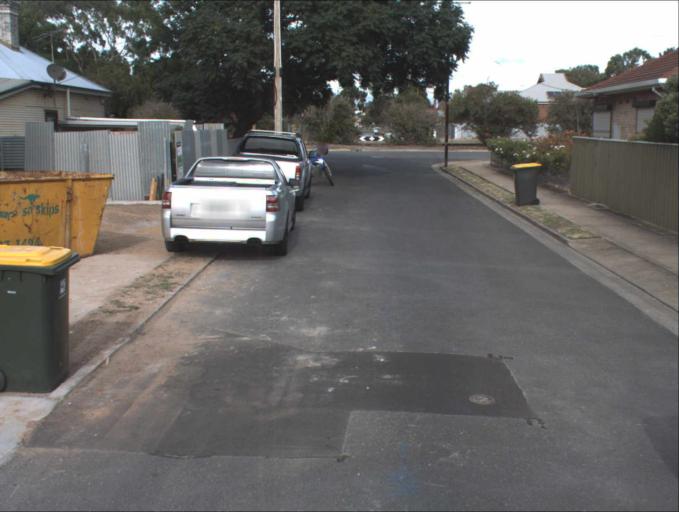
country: AU
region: South Australia
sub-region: Port Adelaide Enfield
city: Birkenhead
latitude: -34.8288
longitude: 138.4921
